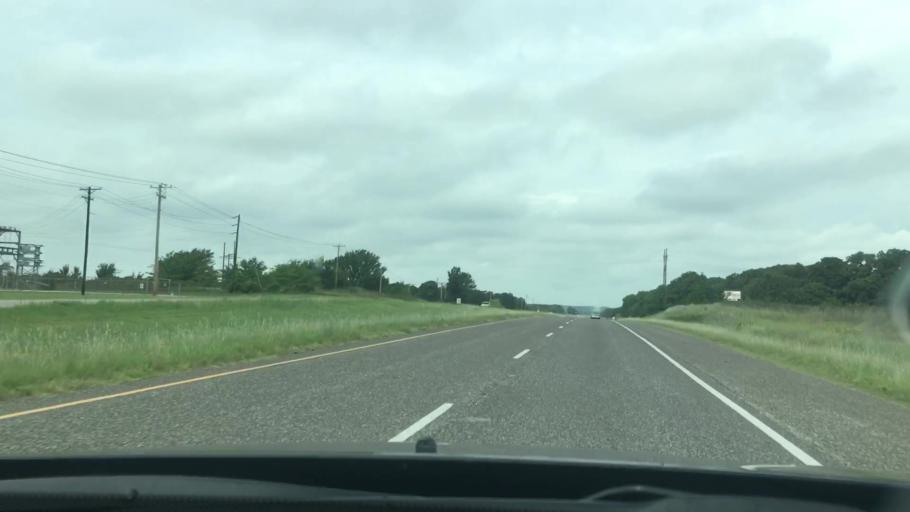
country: US
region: Oklahoma
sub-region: Carter County
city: Lone Grove
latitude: 34.1730
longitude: -97.3315
